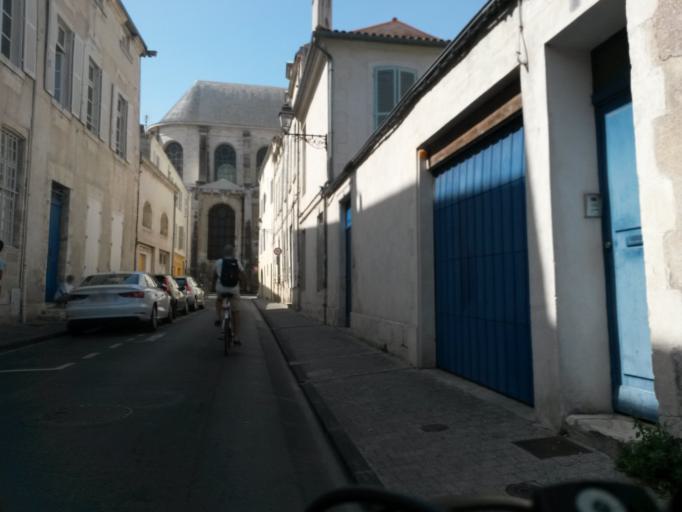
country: FR
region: Poitou-Charentes
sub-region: Departement de la Charente-Maritime
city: La Rochelle
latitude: 46.1612
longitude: -1.1523
